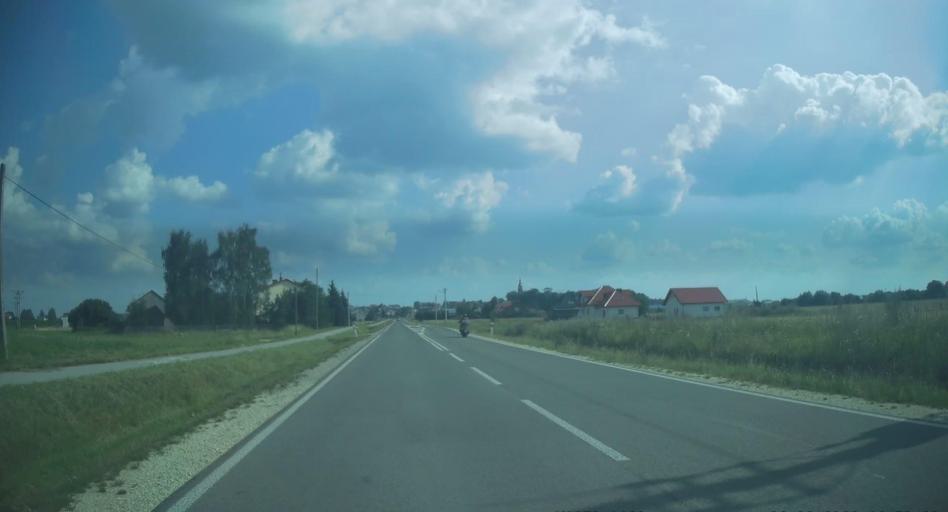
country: PL
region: Swietokrzyskie
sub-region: Powiat kielecki
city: Lopuszno
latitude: 50.9568
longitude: 20.2497
